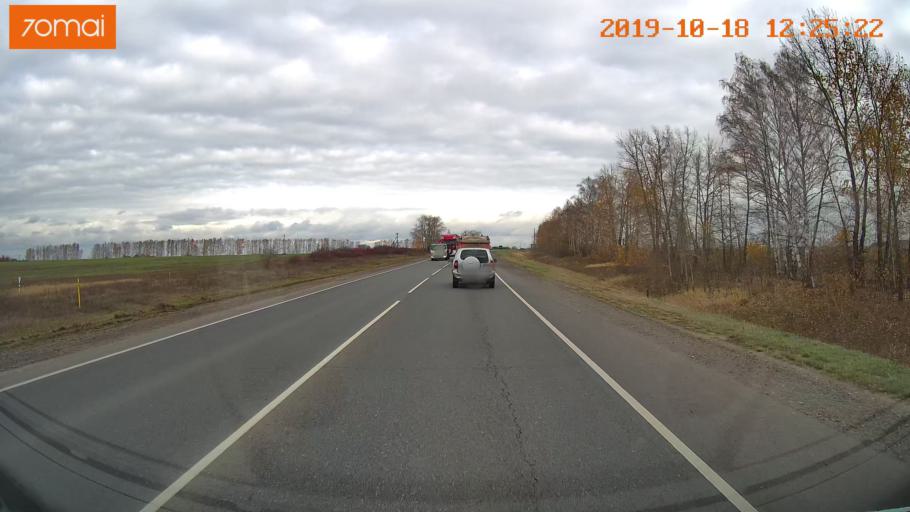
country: RU
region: Rjazan
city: Rybnoye
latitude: 54.5492
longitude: 39.5197
